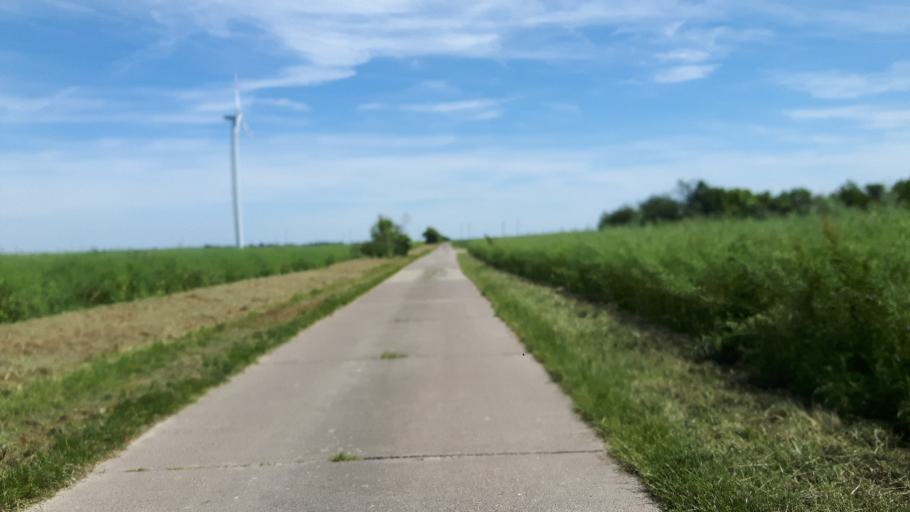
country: DE
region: Saxony-Anhalt
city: Kropstadt
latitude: 52.0037
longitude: 12.7435
